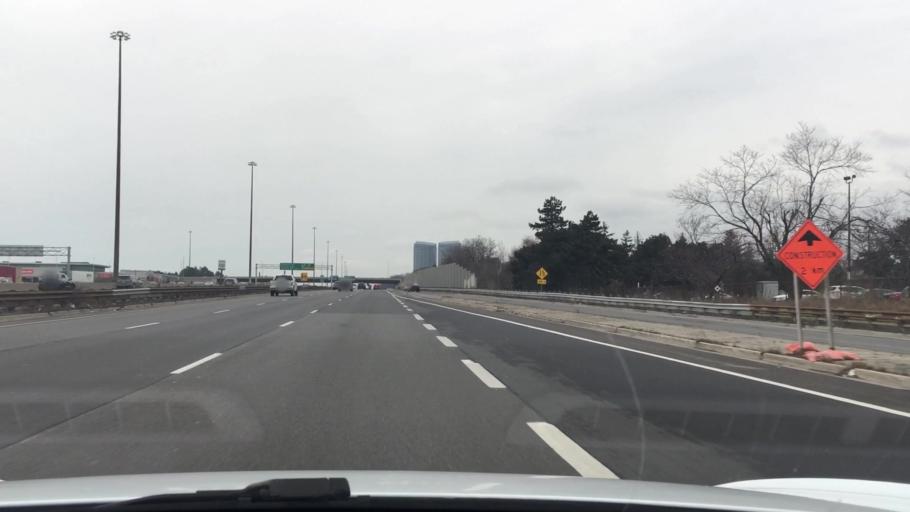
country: CA
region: Ontario
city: Scarborough
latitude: 43.7814
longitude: -79.2578
